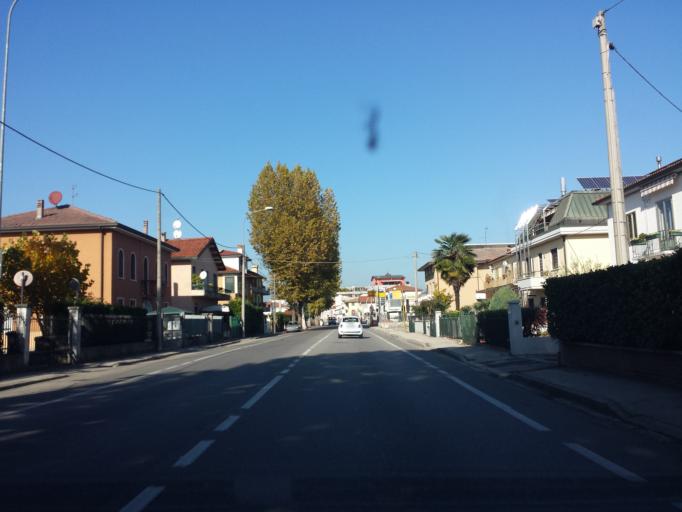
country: IT
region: Veneto
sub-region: Provincia di Vicenza
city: Crispi Cavour
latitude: 45.5656
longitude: 11.5159
